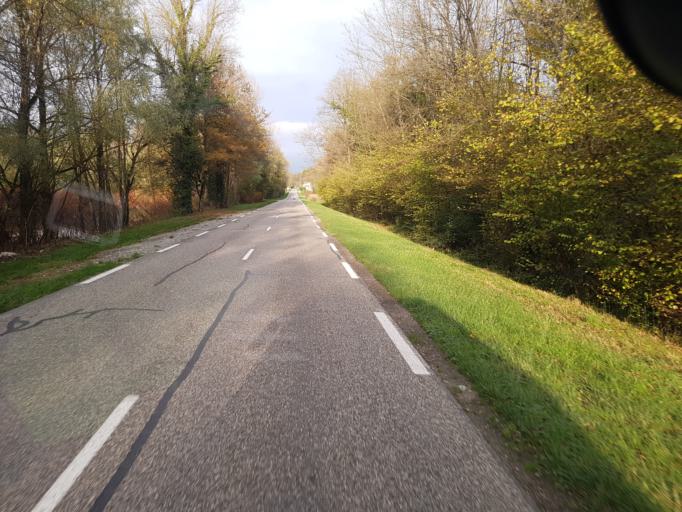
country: FR
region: Rhone-Alpes
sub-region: Departement de la Haute-Savoie
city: Frangy
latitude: 45.9984
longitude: 5.8551
